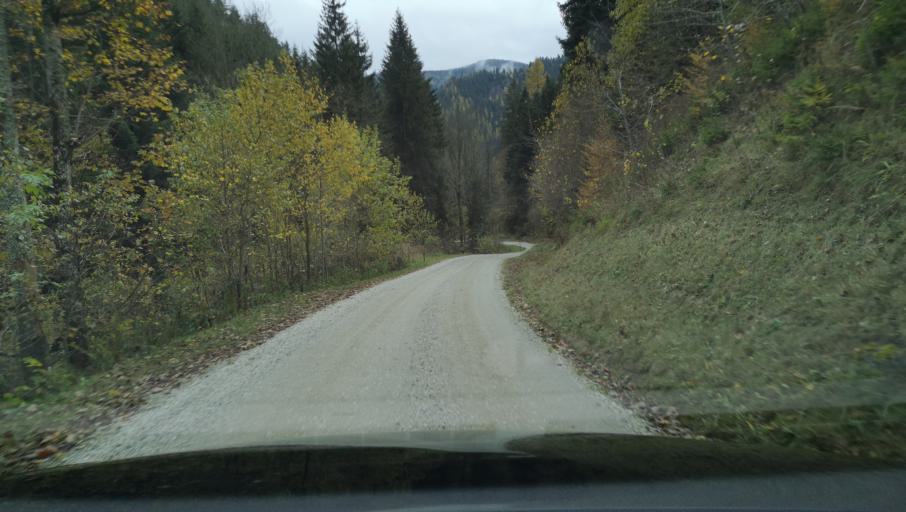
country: AT
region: Styria
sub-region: Politischer Bezirk Weiz
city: Birkfeld
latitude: 47.3738
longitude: 15.6282
